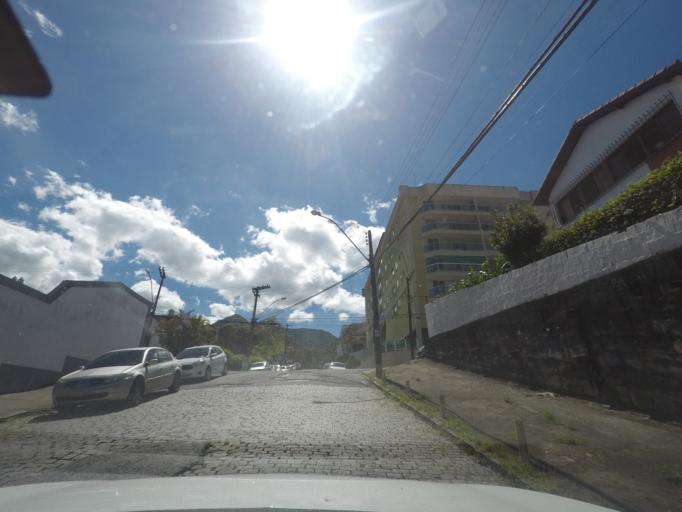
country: BR
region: Rio de Janeiro
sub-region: Teresopolis
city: Teresopolis
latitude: -22.4331
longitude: -42.9795
